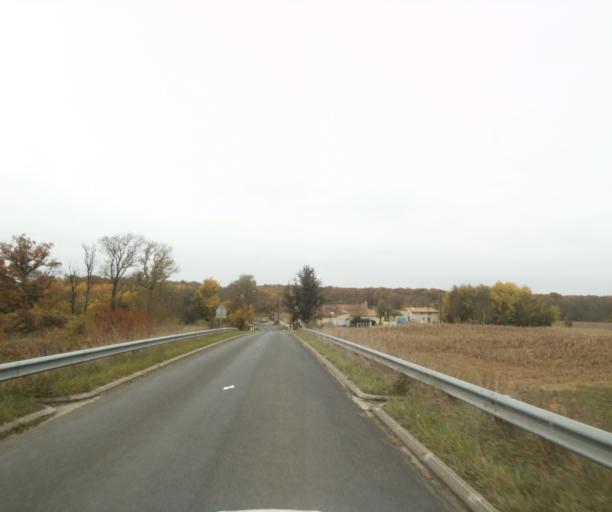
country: FR
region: Poitou-Charentes
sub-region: Departement de la Charente-Maritime
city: Chermignac
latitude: 45.7118
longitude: -0.6936
